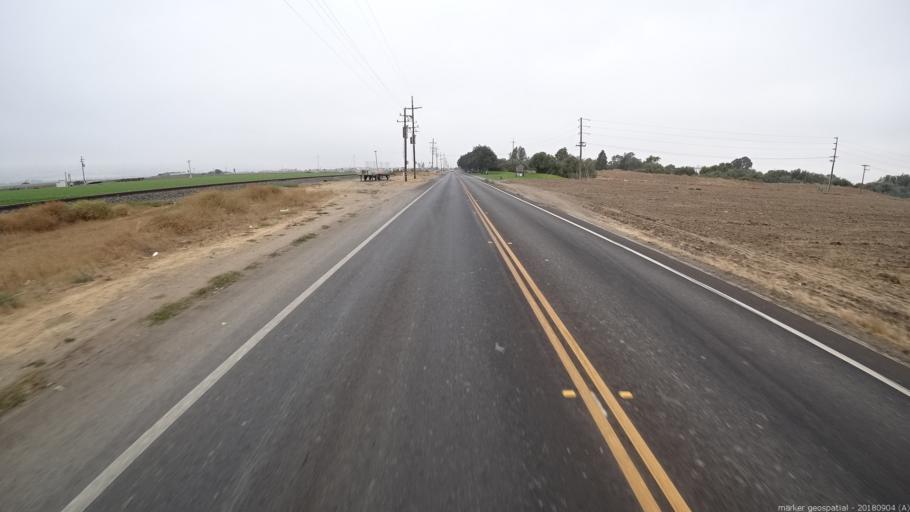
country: US
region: California
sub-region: Monterey County
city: Gonzales
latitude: 36.4960
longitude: -121.4325
